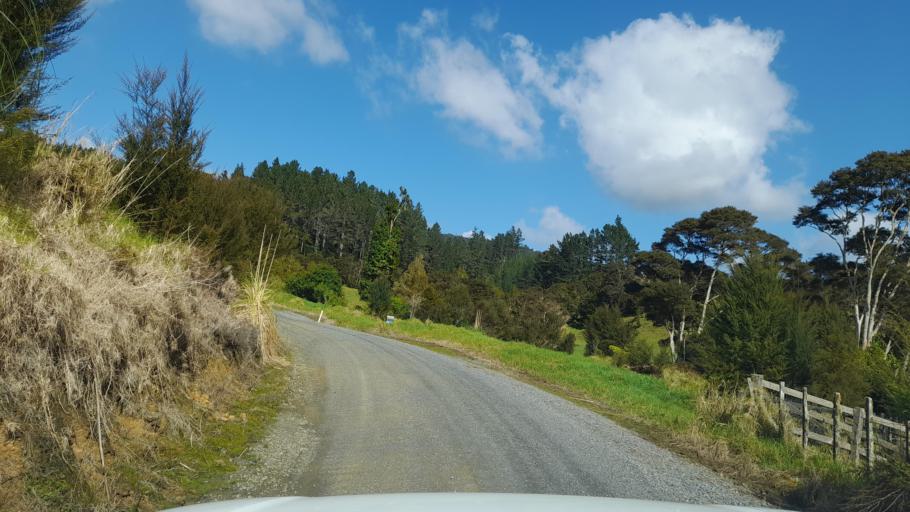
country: NZ
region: Northland
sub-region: Far North District
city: Waimate North
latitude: -35.1565
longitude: 173.7128
